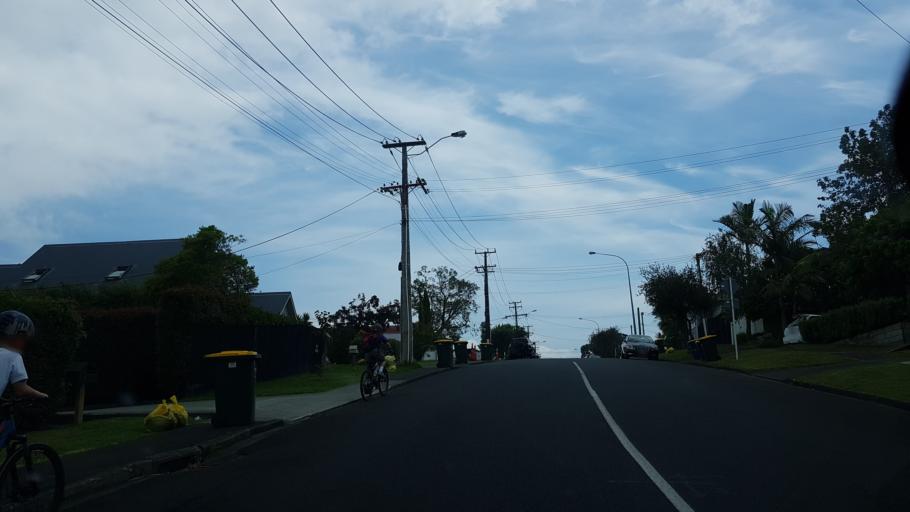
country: NZ
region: Auckland
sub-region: Auckland
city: North Shore
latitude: -36.8062
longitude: 174.7845
